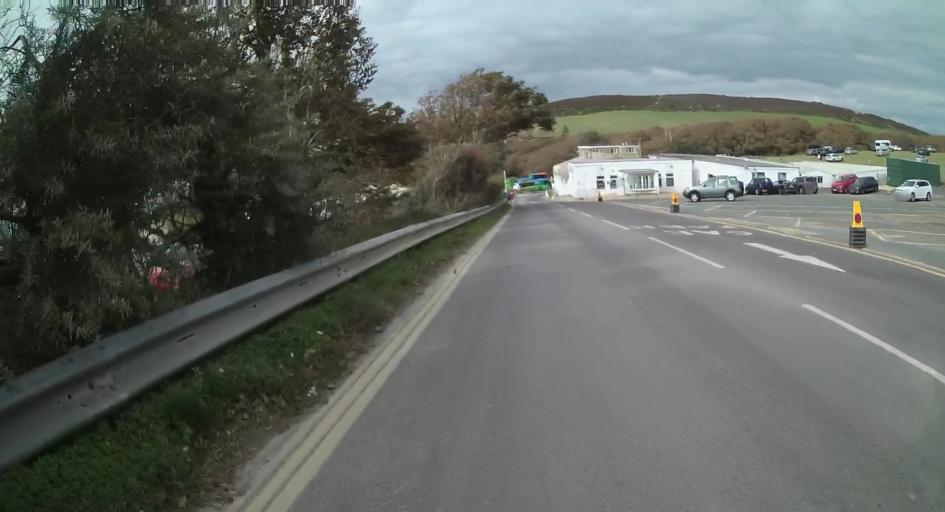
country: GB
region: England
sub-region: Isle of Wight
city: Totland
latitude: 50.6670
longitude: -1.5657
